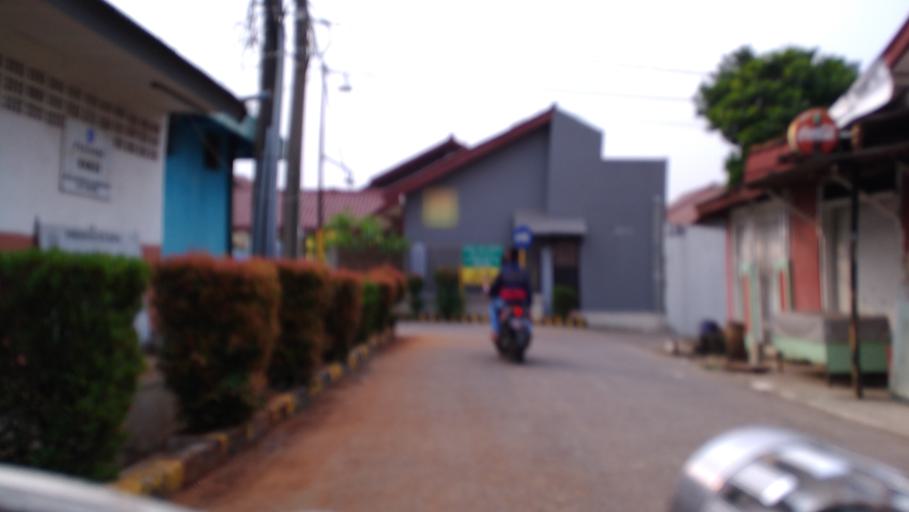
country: ID
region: West Java
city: Depok
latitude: -6.3649
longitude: 106.8637
